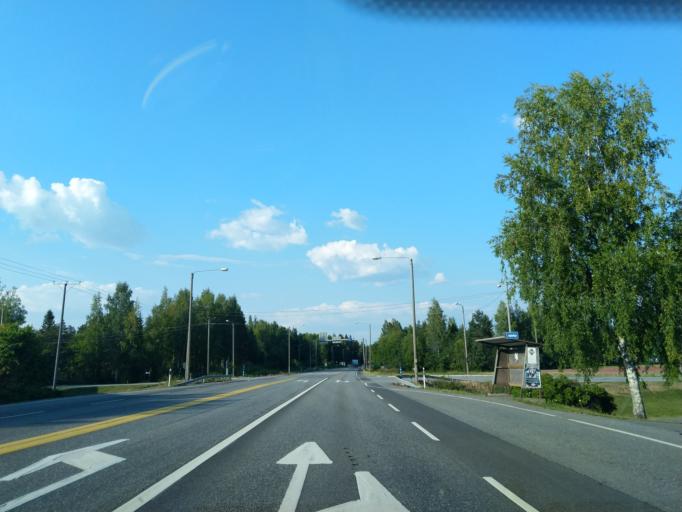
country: FI
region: Satakunta
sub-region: Pori
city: Pomarkku
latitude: 61.6994
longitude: 22.0102
